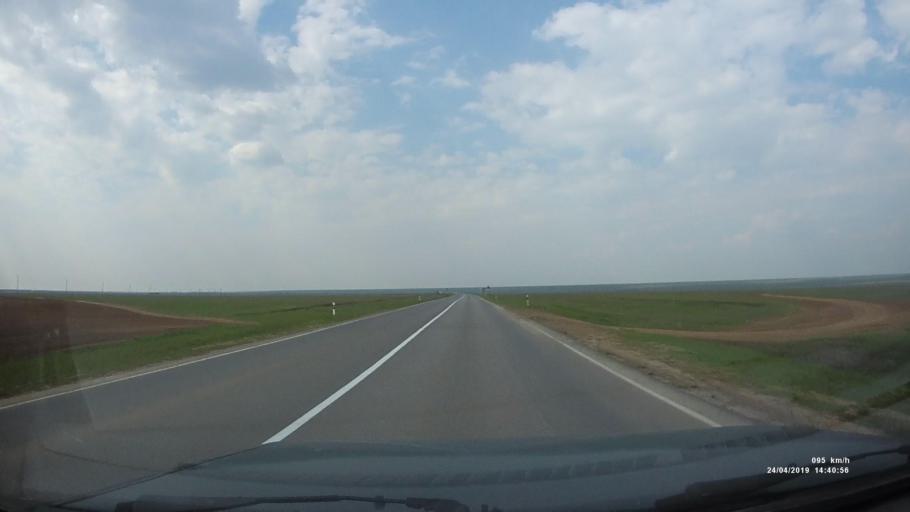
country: RU
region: Rostov
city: Remontnoye
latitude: 46.4390
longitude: 43.8846
